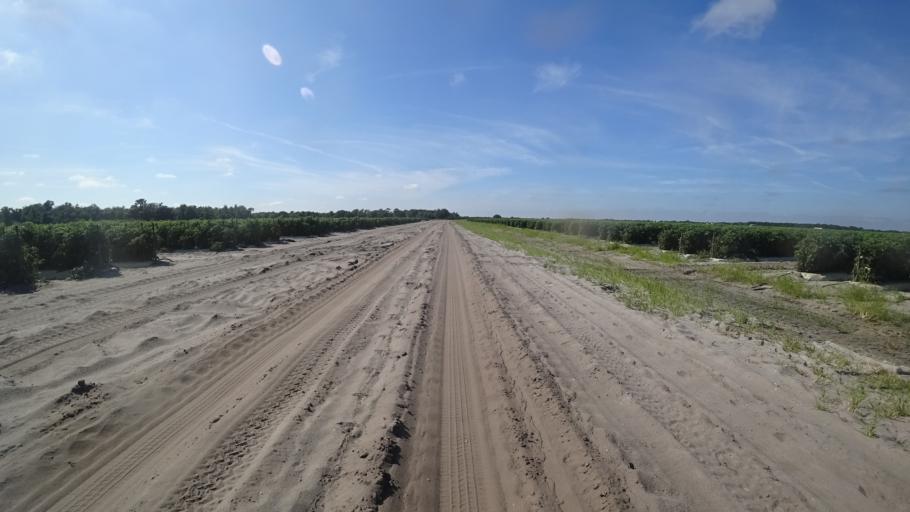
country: US
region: Florida
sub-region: DeSoto County
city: Arcadia
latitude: 27.2947
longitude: -82.0476
